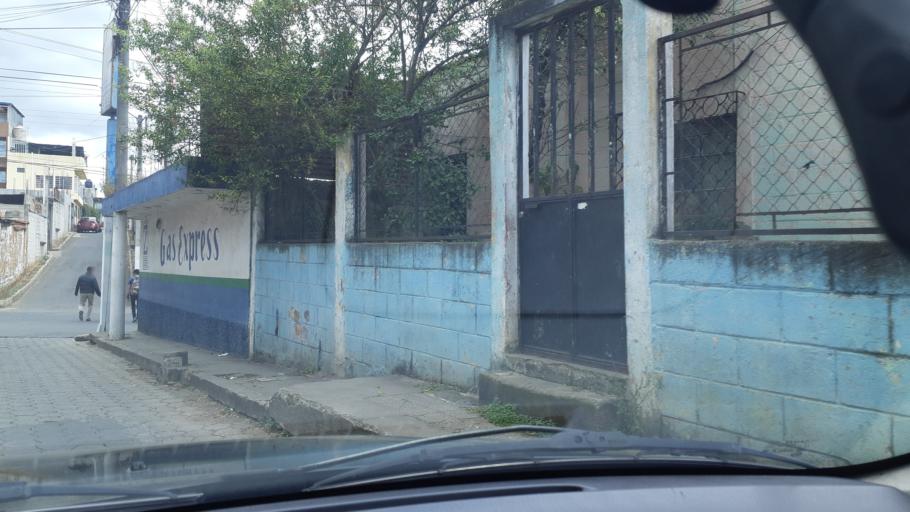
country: GT
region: Chimaltenango
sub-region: Municipio de Chimaltenango
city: Chimaltenango
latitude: 14.6628
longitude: -90.8243
